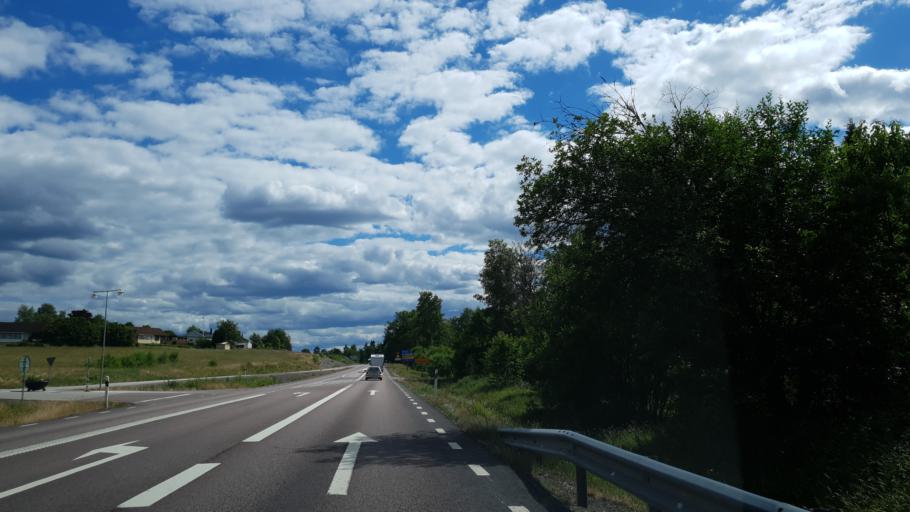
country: SE
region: Kronoberg
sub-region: Lessebo Kommun
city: Lessebo
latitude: 56.8501
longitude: 15.3887
